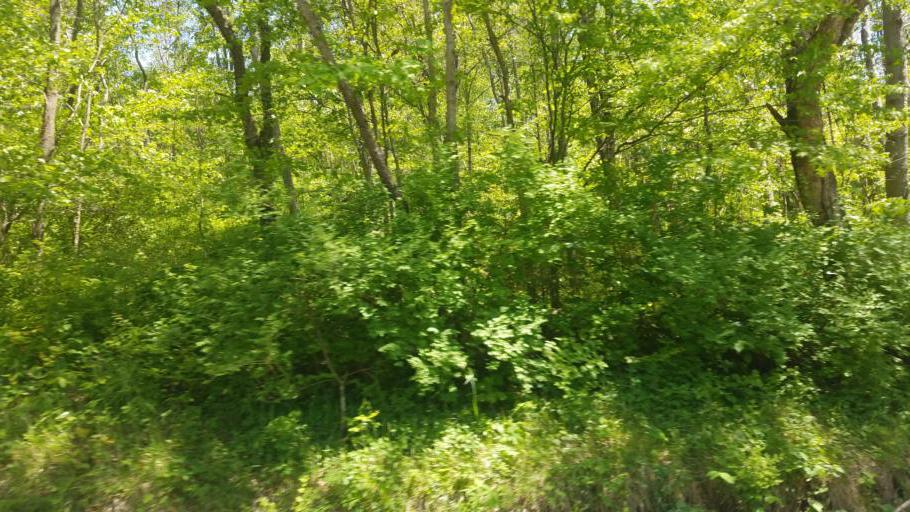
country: US
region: Ohio
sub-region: Licking County
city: Utica
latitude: 40.2380
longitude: -82.2823
